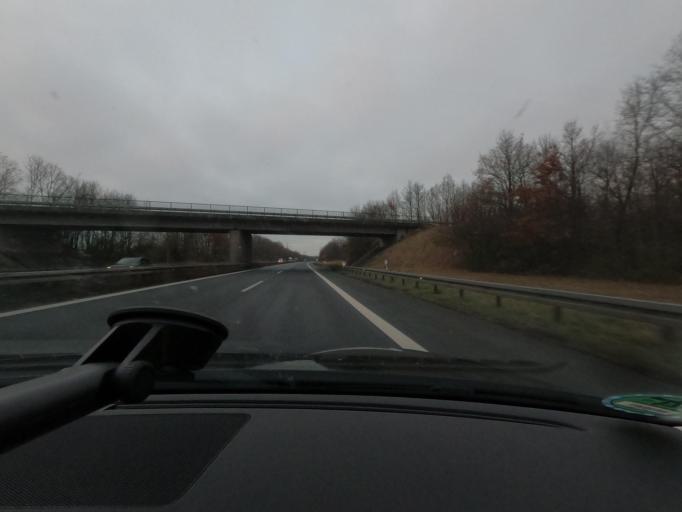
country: DE
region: Bavaria
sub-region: Upper Franconia
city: Buttenheim
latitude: 49.7950
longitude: 11.0257
